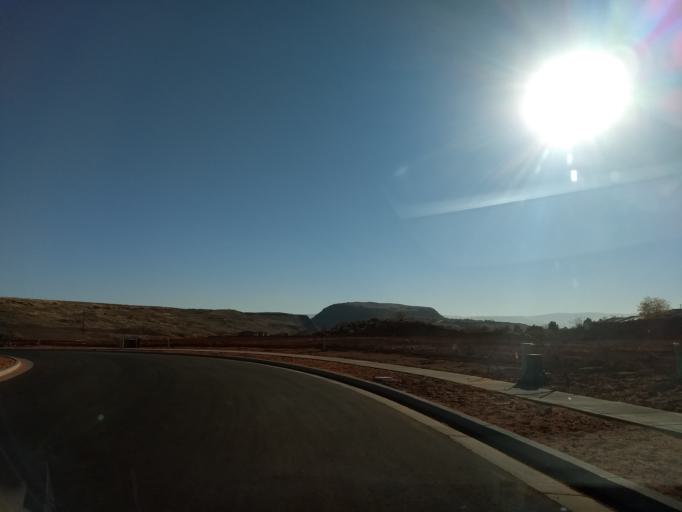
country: US
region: Utah
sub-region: Washington County
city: Washington
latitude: 37.1415
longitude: -113.4805
